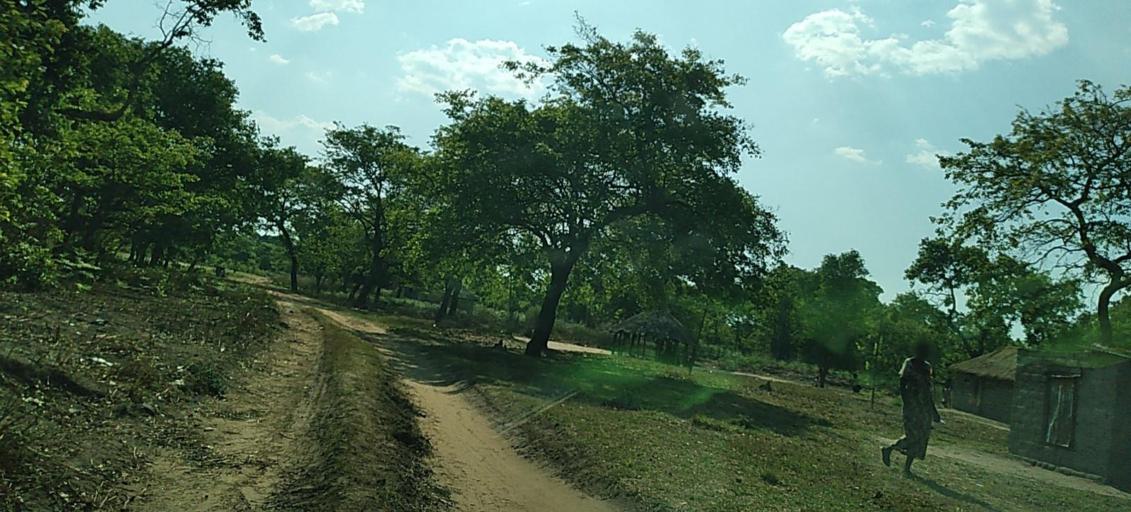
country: ZM
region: North-Western
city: Mwinilunga
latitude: -11.2974
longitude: 24.8593
